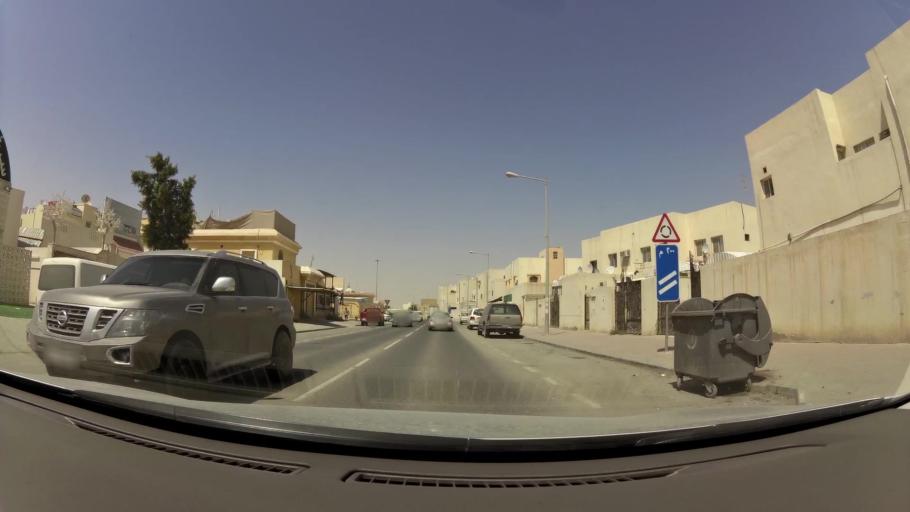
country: QA
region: Baladiyat ar Rayyan
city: Ar Rayyan
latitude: 25.2821
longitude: 51.4078
